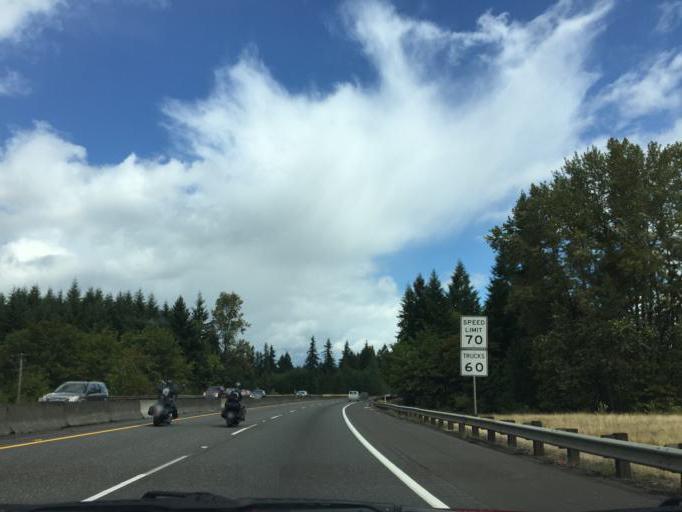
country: US
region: Washington
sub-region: Lewis County
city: Winlock
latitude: 46.3983
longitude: -122.8995
